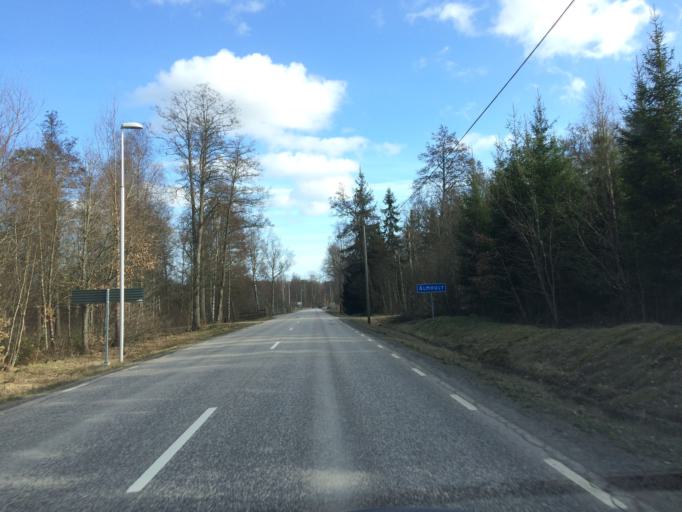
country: SE
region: Kronoberg
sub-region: Almhults Kommun
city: AElmhult
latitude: 56.5679
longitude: 14.1234
